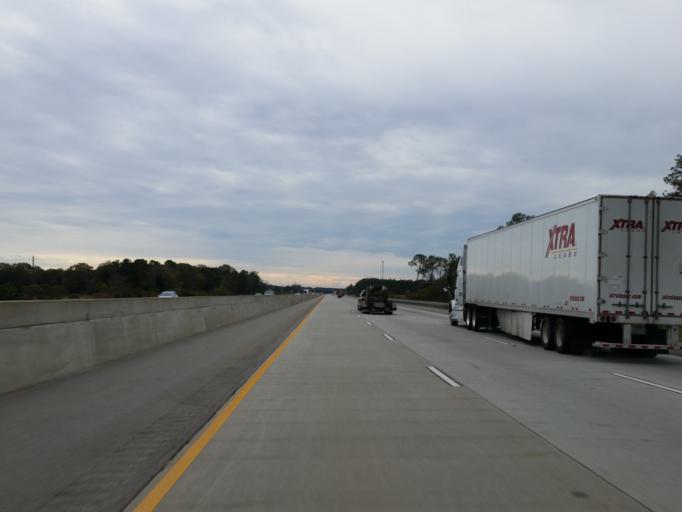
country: US
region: Georgia
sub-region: Tift County
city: Unionville
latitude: 31.3324
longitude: -83.4838
